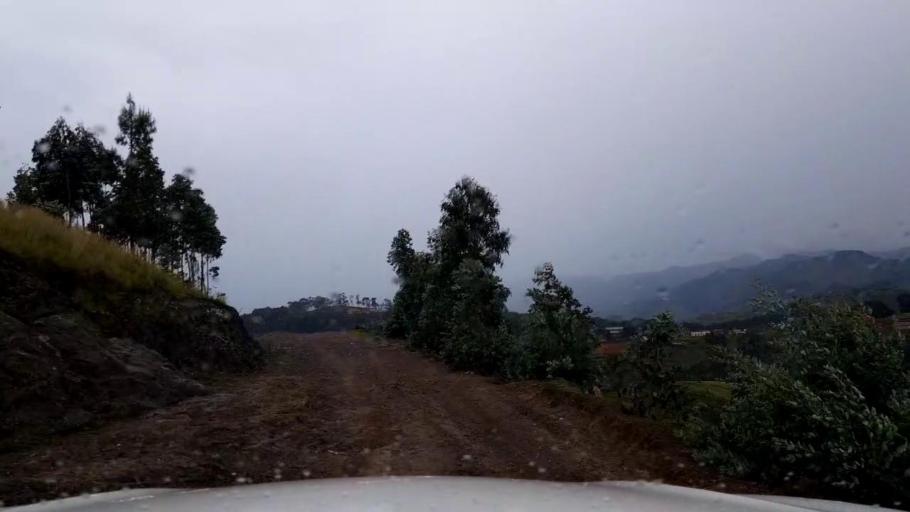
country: RW
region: Western Province
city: Kibuye
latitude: -2.0144
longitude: 29.4688
